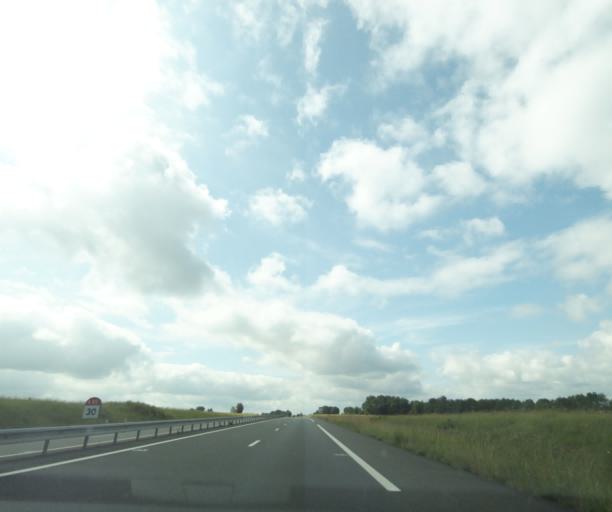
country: FR
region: Pays de la Loire
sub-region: Departement de Maine-et-Loire
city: Saint-Philbert-du-Peuple
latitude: 47.3660
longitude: -0.0835
